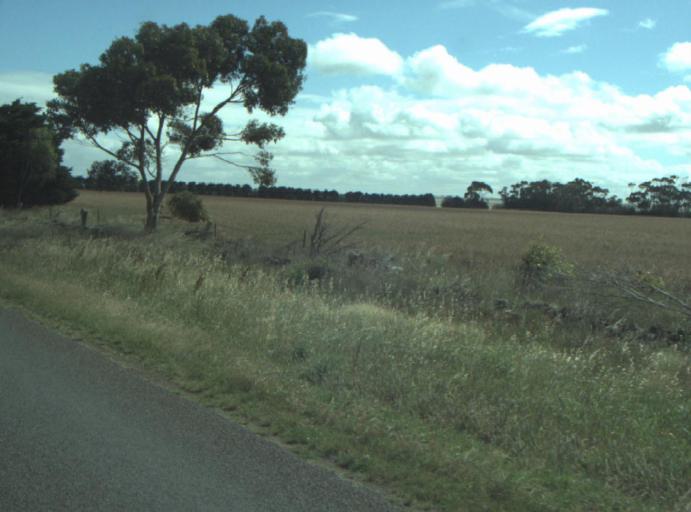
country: AU
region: Victoria
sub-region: Greater Geelong
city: Lara
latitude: -37.9265
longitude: 144.3125
